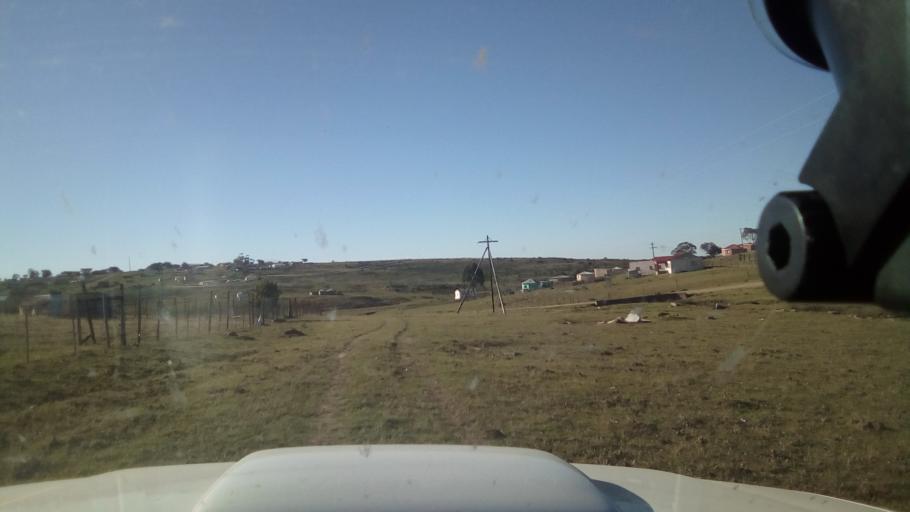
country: ZA
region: Eastern Cape
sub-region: Buffalo City Metropolitan Municipality
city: Bhisho
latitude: -32.9481
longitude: 27.2893
